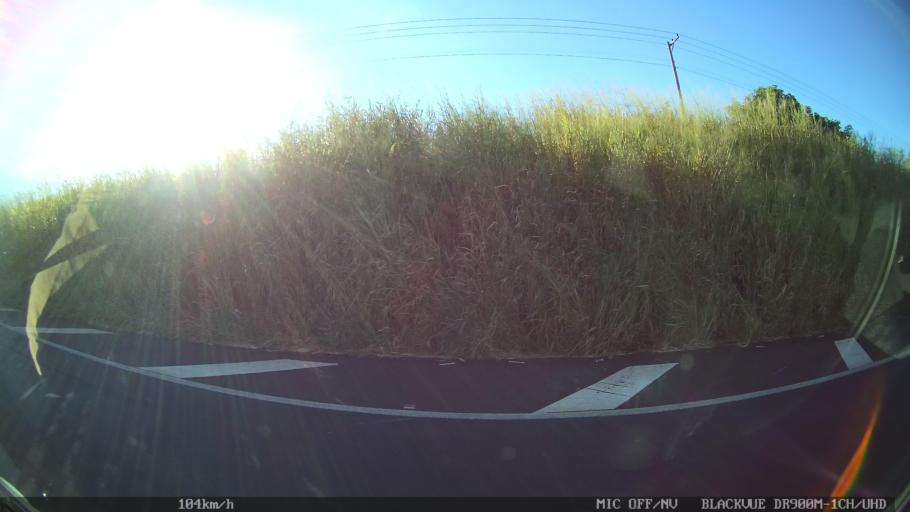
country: BR
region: Sao Paulo
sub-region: Olimpia
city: Olimpia
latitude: -20.7286
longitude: -49.0478
